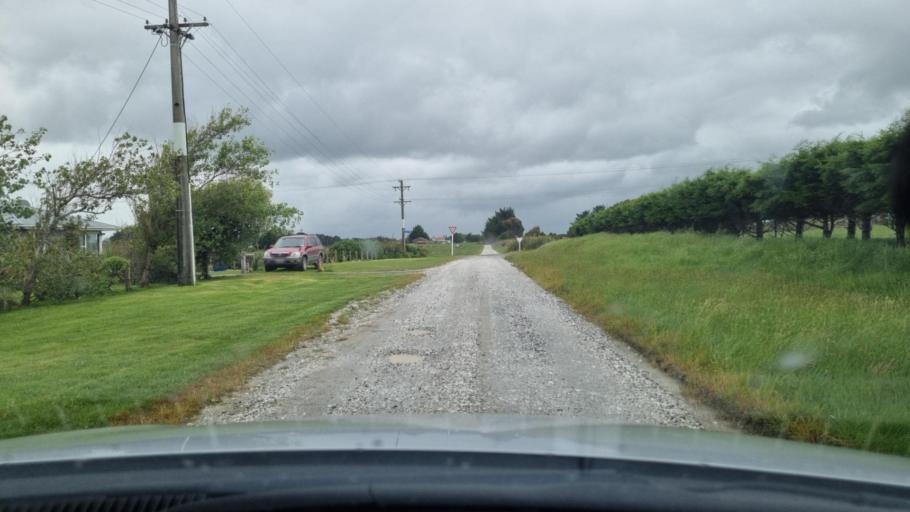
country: NZ
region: Southland
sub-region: Invercargill City
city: Invercargill
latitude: -46.4514
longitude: 168.3939
